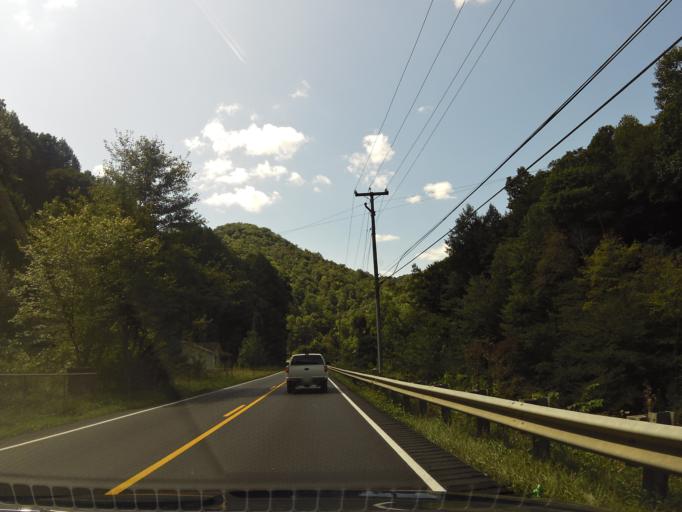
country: US
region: Kentucky
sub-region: Leslie County
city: Hyden
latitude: 37.0197
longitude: -83.3954
